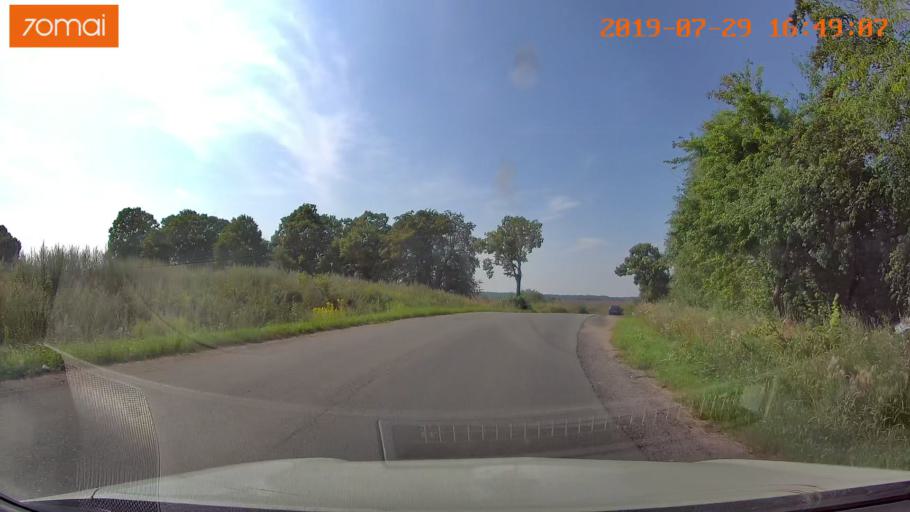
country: RU
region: Kaliningrad
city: Primorsk
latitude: 54.7913
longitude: 20.0684
